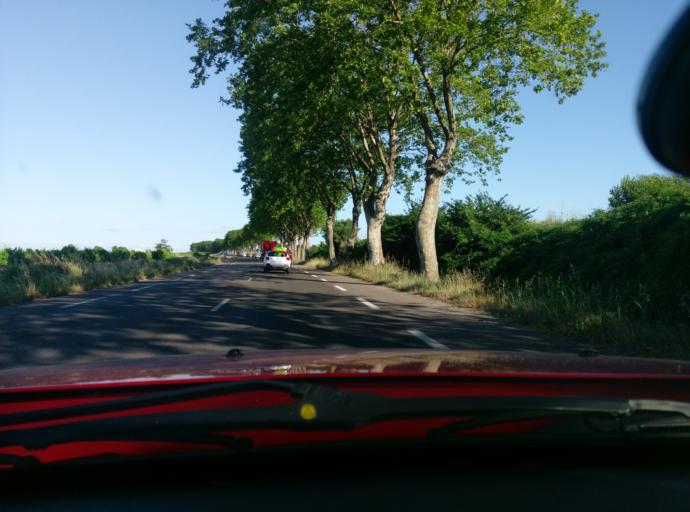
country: FR
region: Languedoc-Roussillon
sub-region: Departement du Gard
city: Uzes
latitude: 43.9838
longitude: 4.4630
